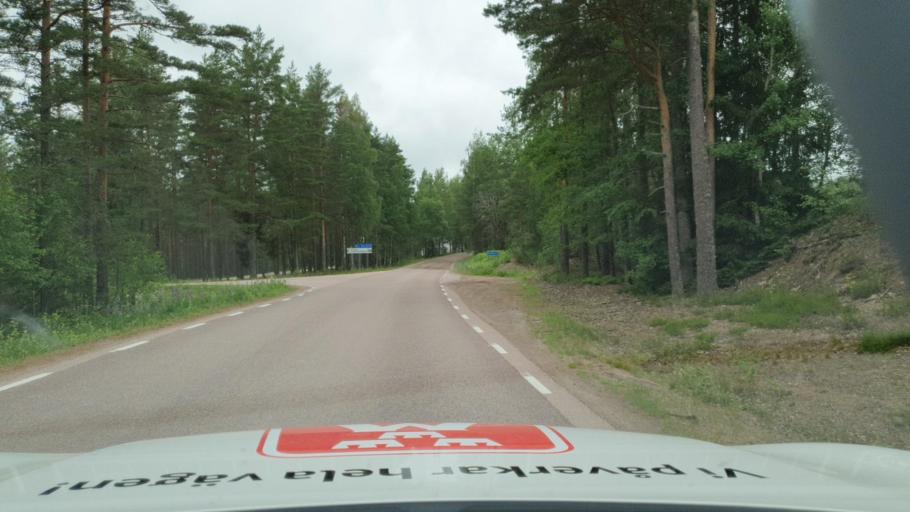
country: SE
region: Vaermland
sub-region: Kristinehamns Kommun
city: Kristinehamn
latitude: 59.5153
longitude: 13.9488
